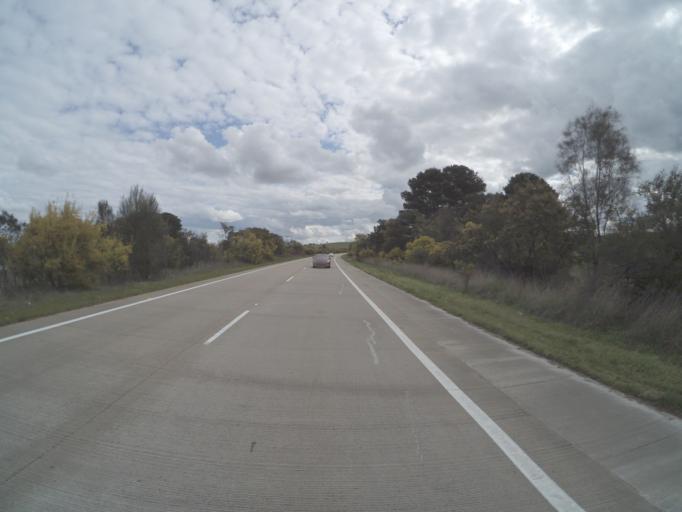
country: AU
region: New South Wales
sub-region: Goulburn Mulwaree
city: Goulburn
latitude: -34.8143
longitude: 149.4669
